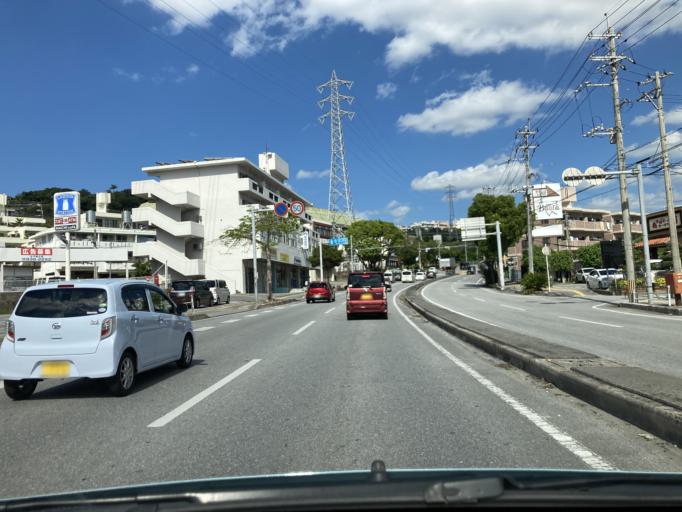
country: JP
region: Okinawa
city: Tomigusuku
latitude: 26.2000
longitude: 127.7143
